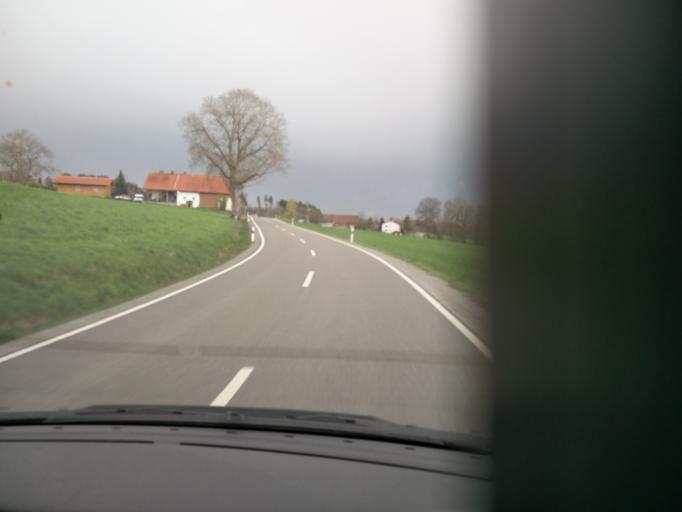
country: DE
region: Bavaria
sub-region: Upper Bavaria
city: Halfing
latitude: 47.9624
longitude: 12.2912
